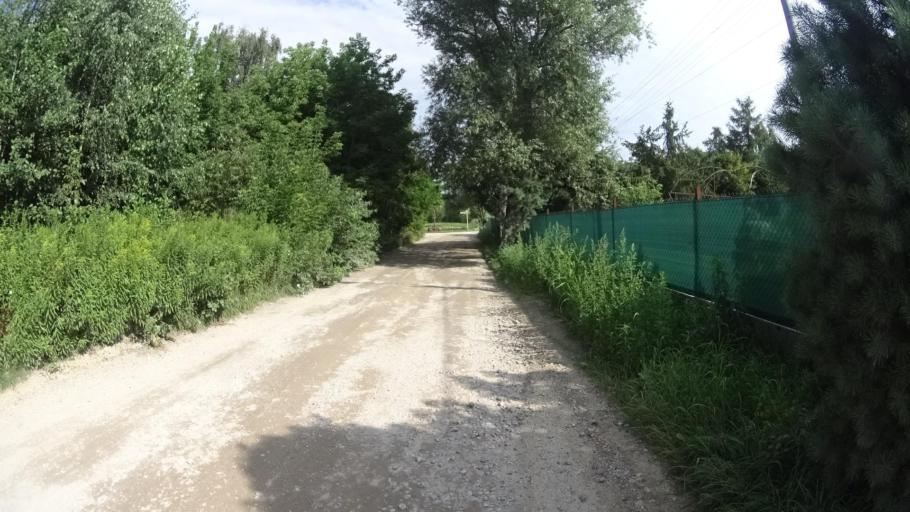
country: PL
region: Masovian Voivodeship
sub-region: Powiat piaseczynski
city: Tarczyn
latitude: 51.9758
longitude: 20.8537
